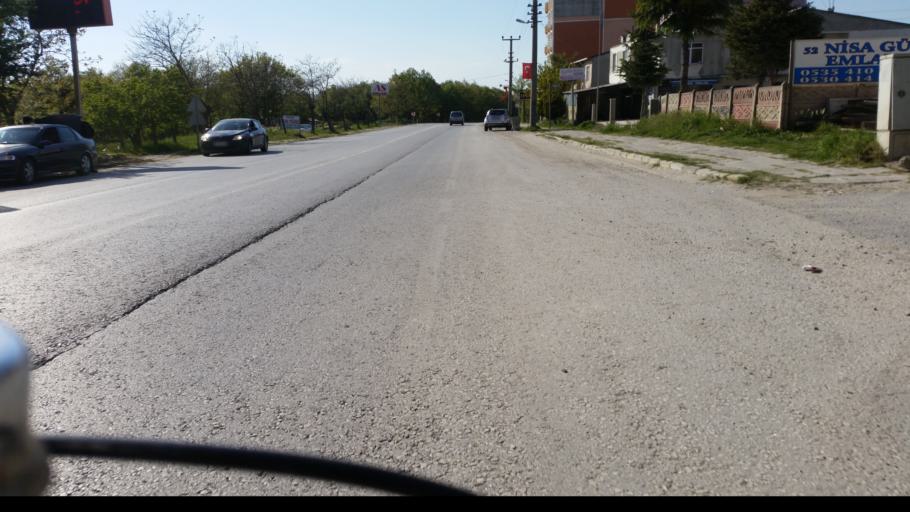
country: TR
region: Tekirdag
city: Saray
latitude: 41.3598
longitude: 27.9463
